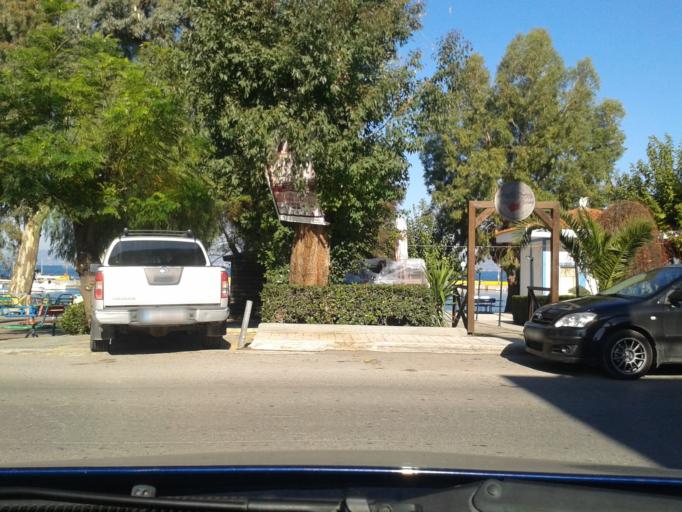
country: GR
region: Attica
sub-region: Nomarchia Anatolikis Attikis
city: Nea Palatia
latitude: 38.3215
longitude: 23.7950
